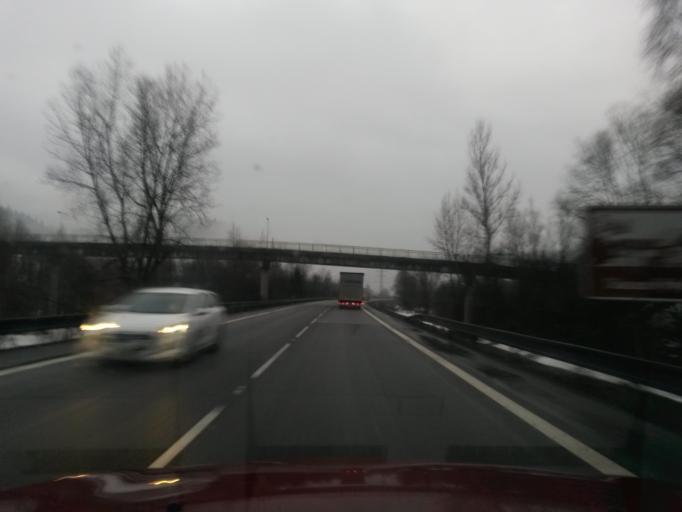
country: SK
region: Zilinsky
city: Kysucke Nove Mesto
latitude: 49.3630
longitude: 18.8320
